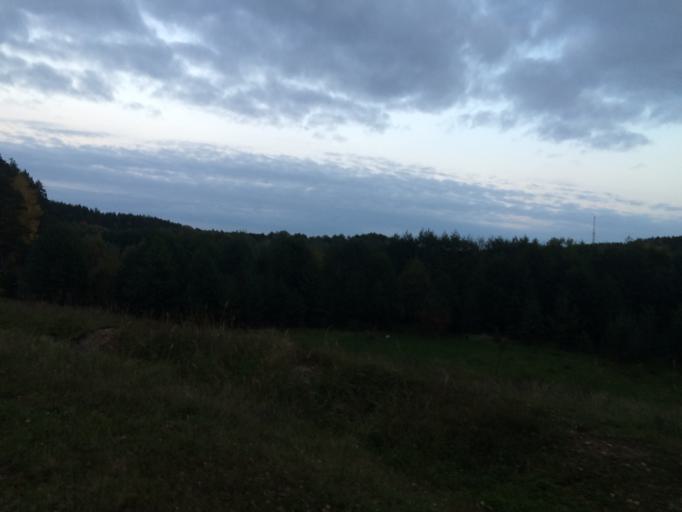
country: RU
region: Nizjnij Novgorod
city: Sarov
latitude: 54.9414
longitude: 43.3413
